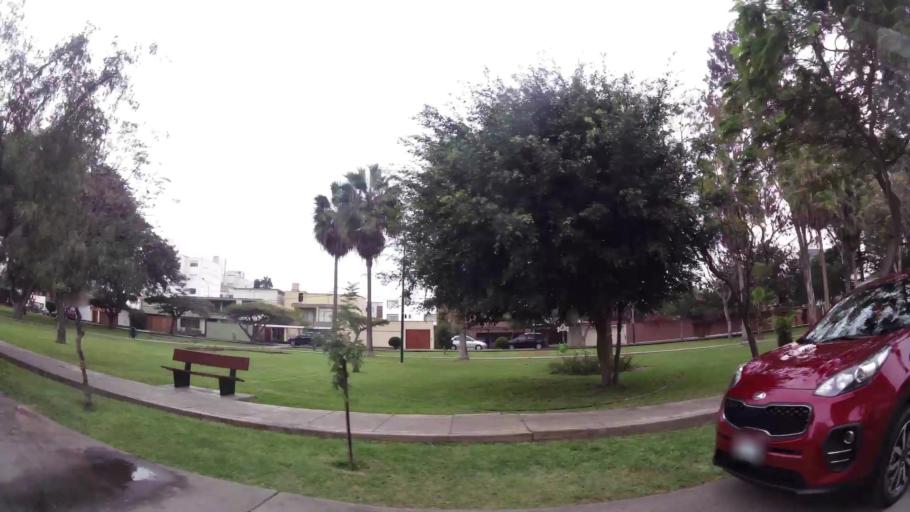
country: PE
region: Lima
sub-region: Lima
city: Surco
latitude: -12.1220
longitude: -76.9915
